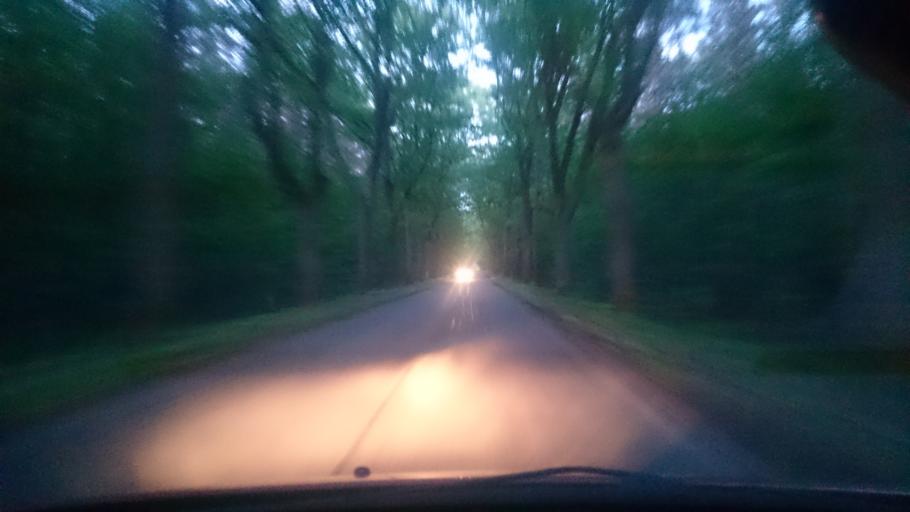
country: PL
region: Opole Voivodeship
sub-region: Powiat opolski
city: Ozimek
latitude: 50.6687
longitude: 18.1762
